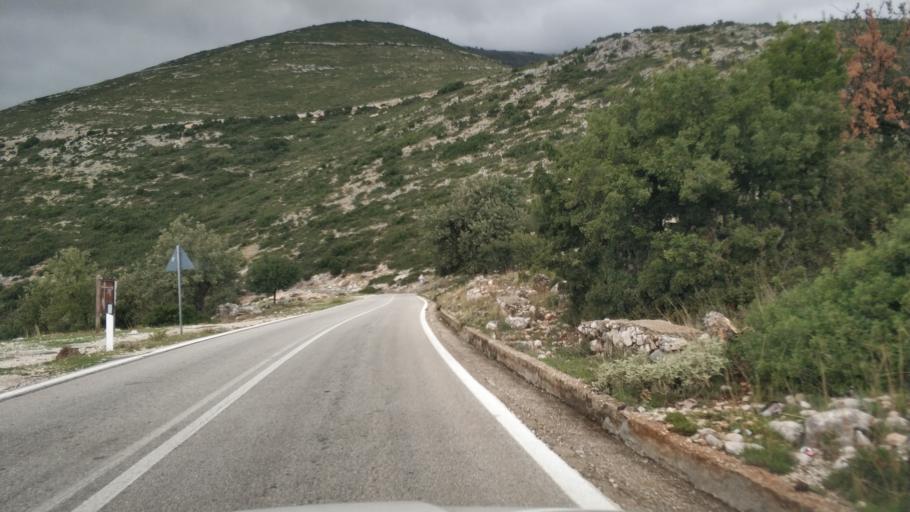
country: AL
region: Vlore
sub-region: Rrethi i Vlores
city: Vranisht
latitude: 40.1756
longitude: 19.6052
